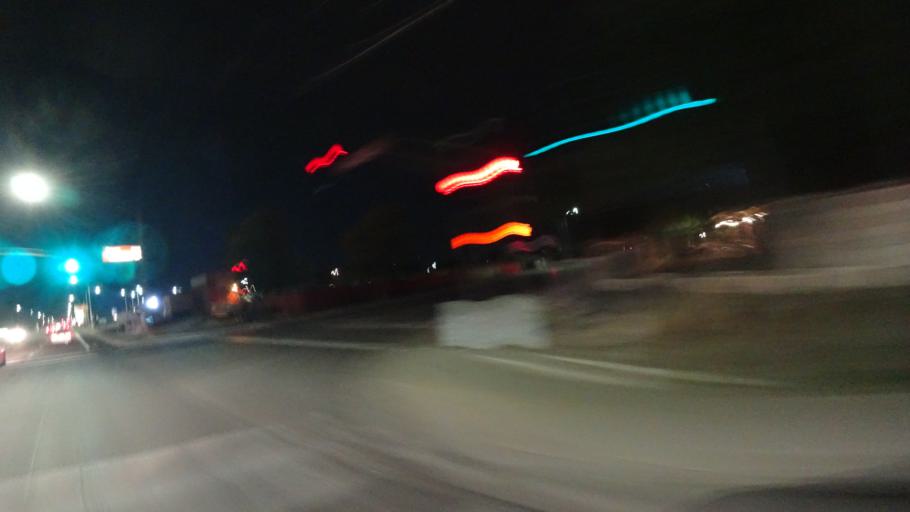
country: US
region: Arizona
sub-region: Maricopa County
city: Chandler
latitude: 33.3061
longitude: -111.8331
